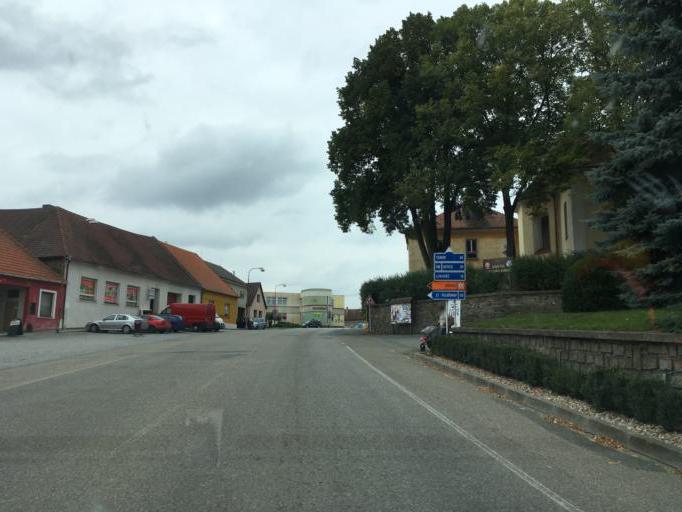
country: CZ
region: Central Bohemia
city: Cechtice
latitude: 49.6231
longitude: 15.0488
